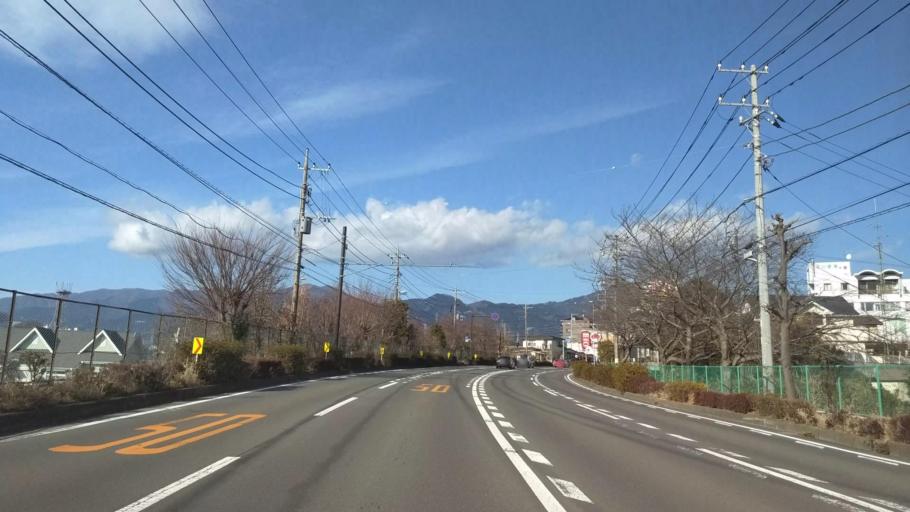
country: JP
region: Kanagawa
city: Hadano
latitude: 35.3727
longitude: 139.2352
